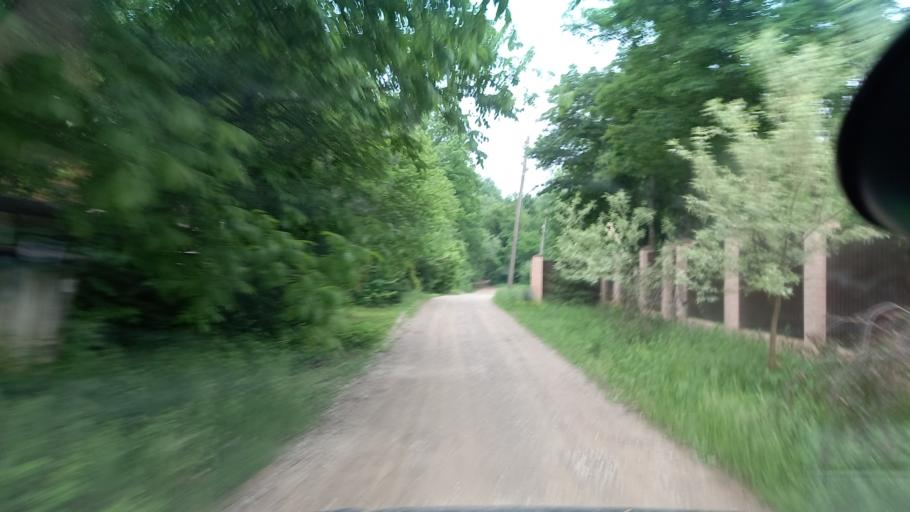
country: RU
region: Krasnodarskiy
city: Azovskaya
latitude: 44.6364
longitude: 38.6190
